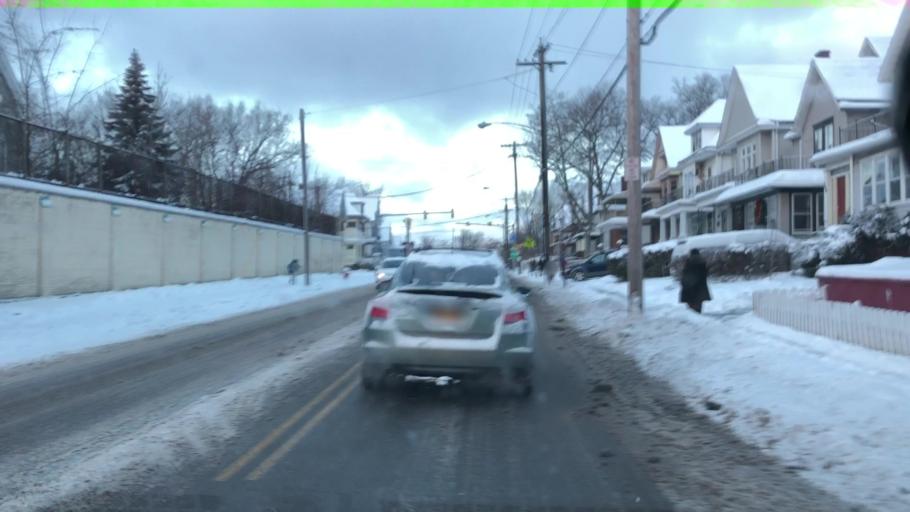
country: US
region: New York
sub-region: Erie County
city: Buffalo
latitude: 42.9039
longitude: -78.8492
